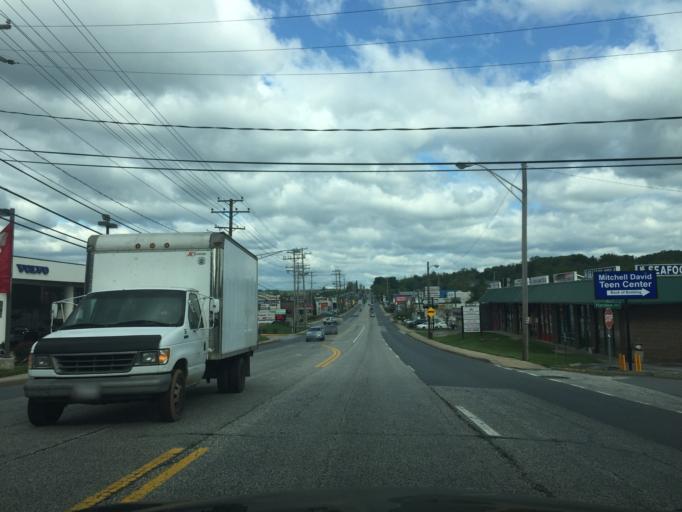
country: US
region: Maryland
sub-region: Baltimore County
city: Garrison
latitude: 39.4042
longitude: -76.7582
